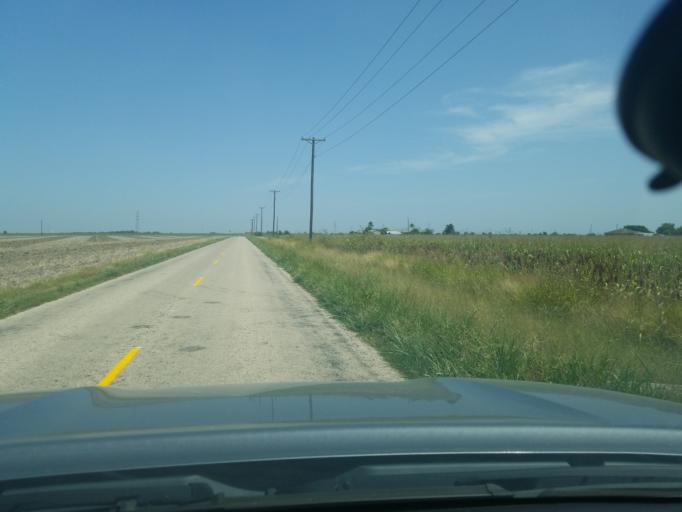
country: US
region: Texas
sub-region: Guadalupe County
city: Lake Dunlap
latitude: 29.6779
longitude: -98.0252
